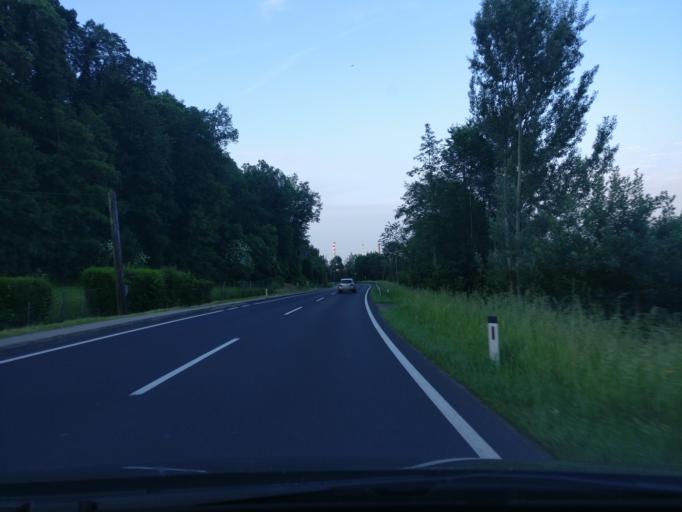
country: AT
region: Upper Austria
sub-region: Politischer Bezirk Urfahr-Umgebung
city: Steyregg
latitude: 48.2981
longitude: 14.3428
